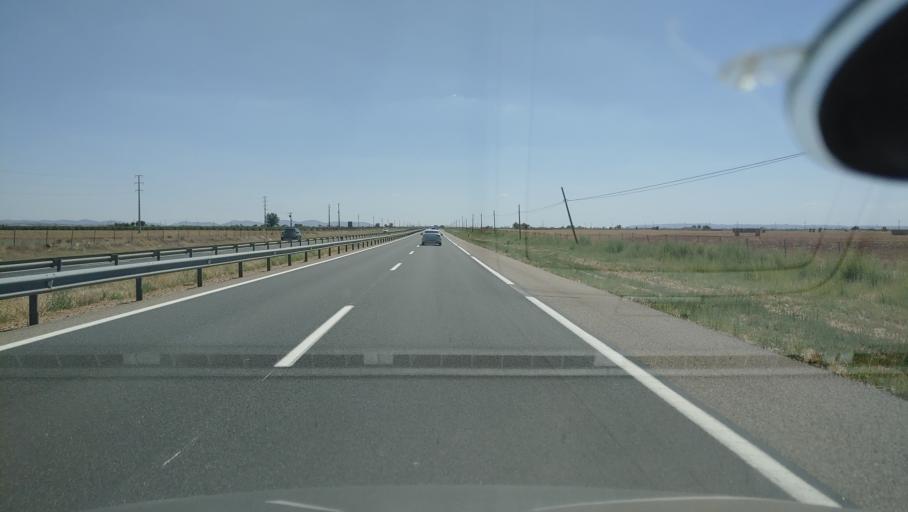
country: ES
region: Castille-La Mancha
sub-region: Provincia de Ciudad Real
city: Manzanares
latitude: 39.0991
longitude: -3.3771
